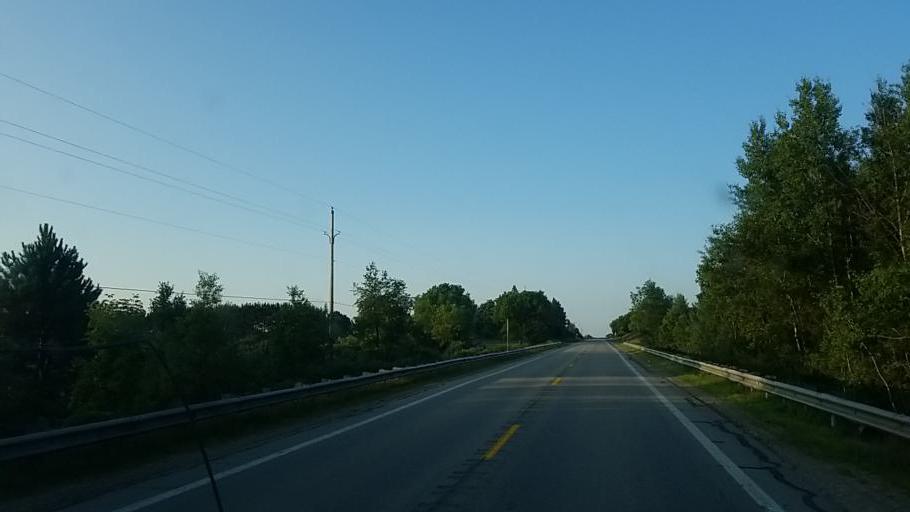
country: US
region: Michigan
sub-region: Isabella County
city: Lake Isabella
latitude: 43.6213
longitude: -85.1459
